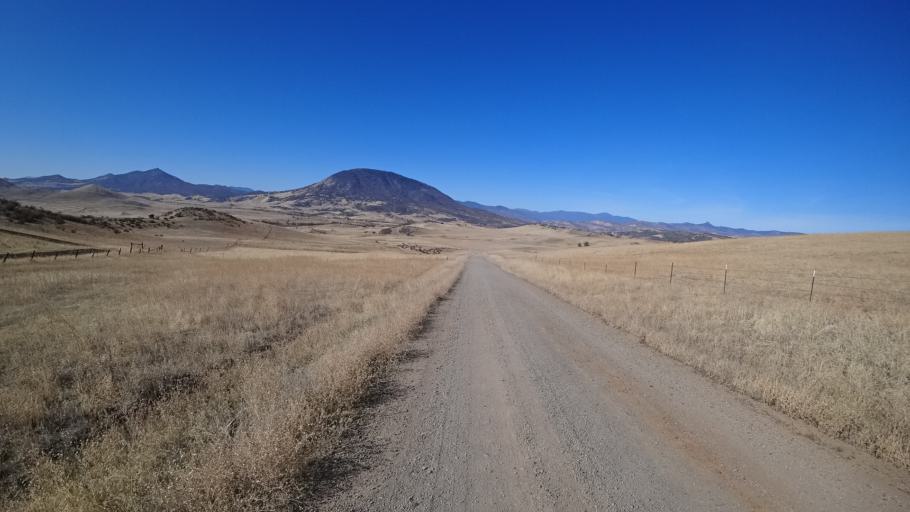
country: US
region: California
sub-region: Siskiyou County
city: Montague
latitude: 41.8446
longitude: -122.4292
